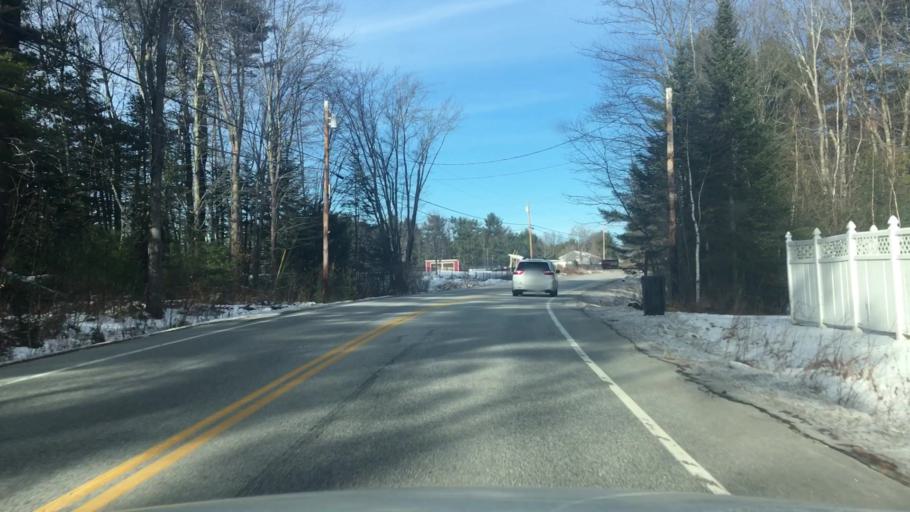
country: US
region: Maine
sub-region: Androscoggin County
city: Lisbon
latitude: 43.9700
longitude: -70.1244
